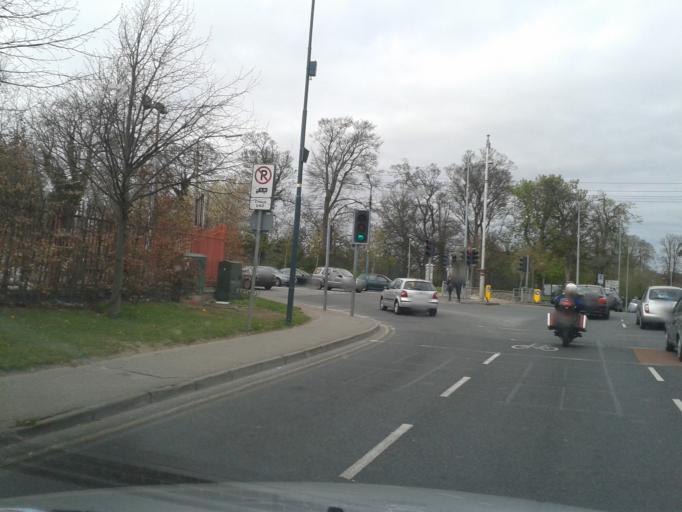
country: IE
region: Leinster
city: Beaumont
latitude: 53.3970
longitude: -6.2452
